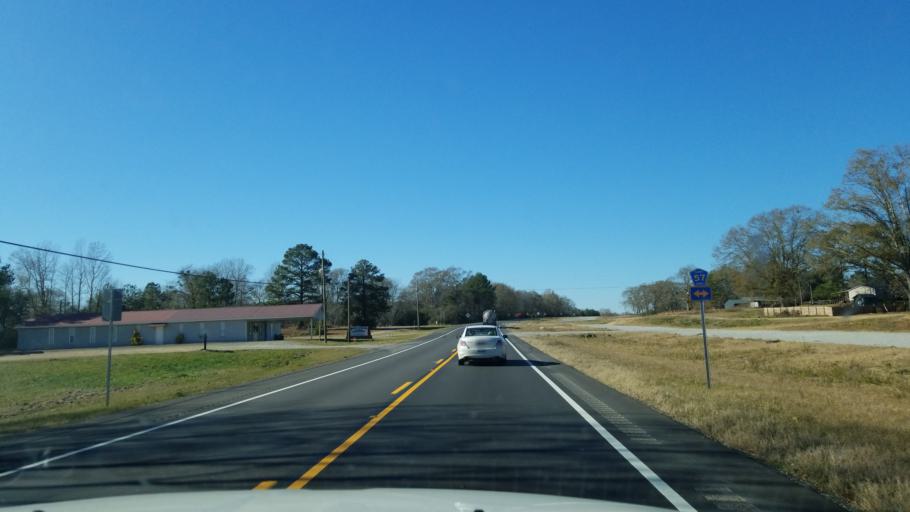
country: US
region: Alabama
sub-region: Pickens County
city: Gordo
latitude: 33.3352
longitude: -87.9282
